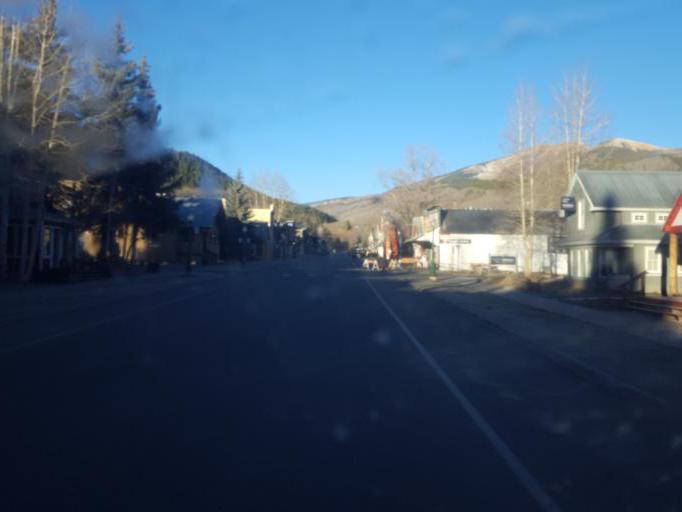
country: US
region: Colorado
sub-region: Gunnison County
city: Crested Butte
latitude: 38.8698
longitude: -106.9834
